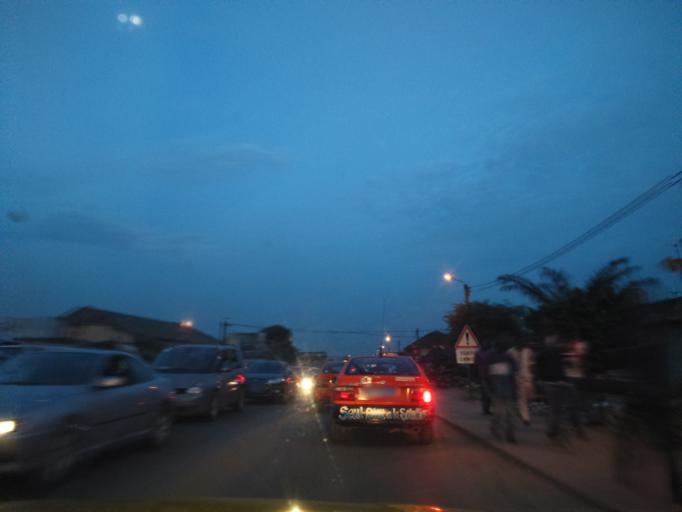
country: CI
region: Lagunes
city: Abobo
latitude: 5.4089
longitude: -3.9928
